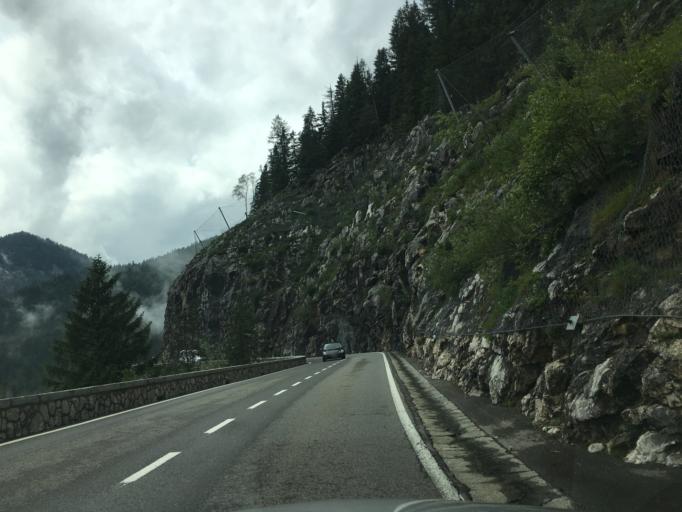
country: AT
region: Tyrol
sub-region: Politischer Bezirk Reutte
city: Nesselwangle
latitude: 47.4520
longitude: 10.6284
